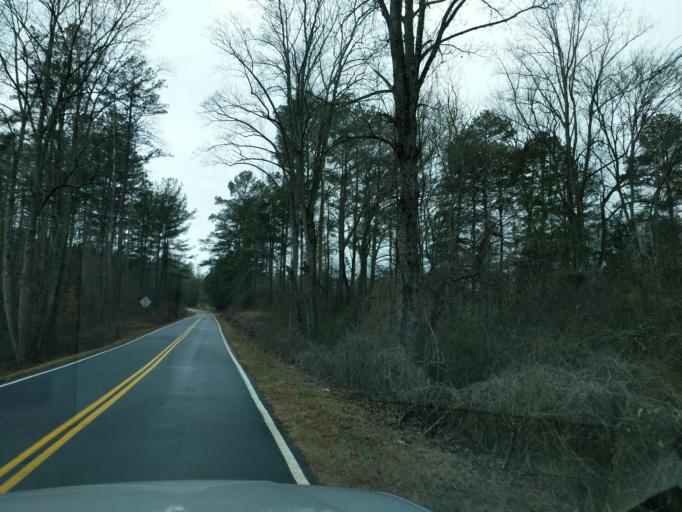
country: US
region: South Carolina
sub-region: Oconee County
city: Walhalla
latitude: 34.7945
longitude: -83.0965
